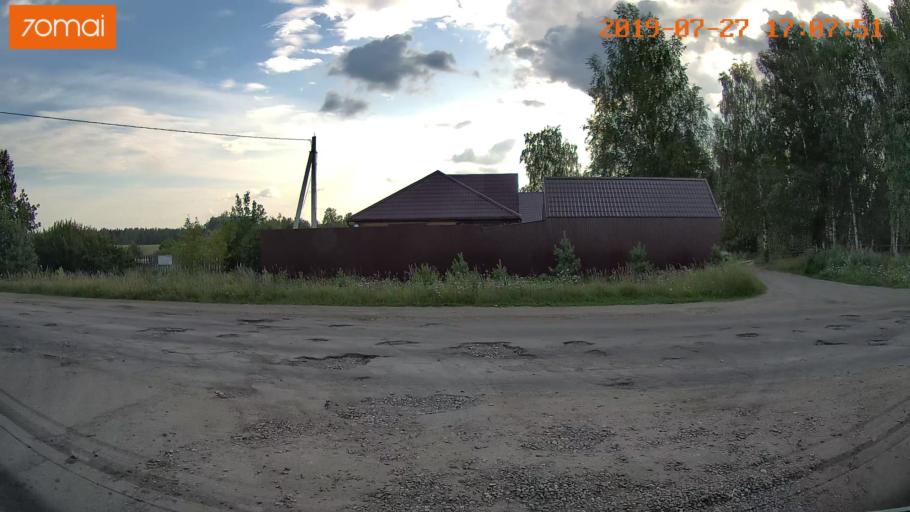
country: RU
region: Ivanovo
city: Novo-Talitsy
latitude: 57.0844
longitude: 40.8355
